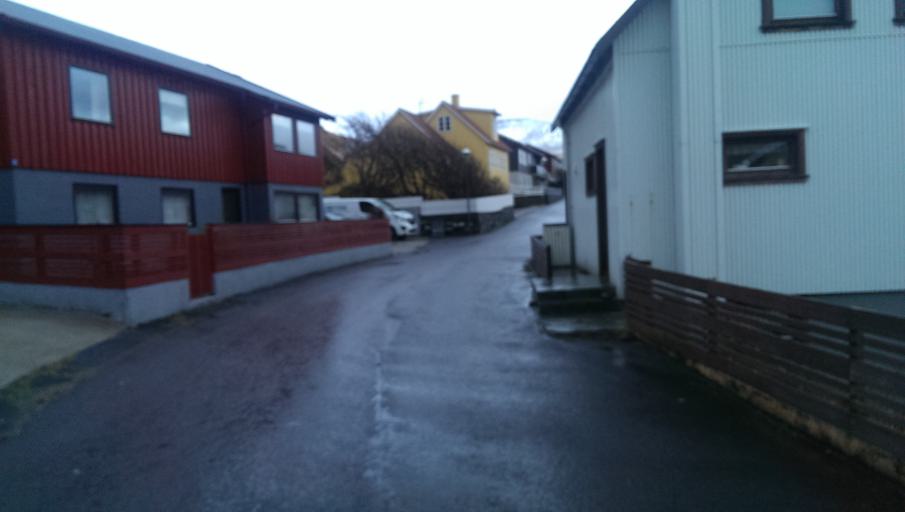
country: FO
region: Eysturoy
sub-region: Eidi
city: Eidi
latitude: 62.3000
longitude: -7.0873
